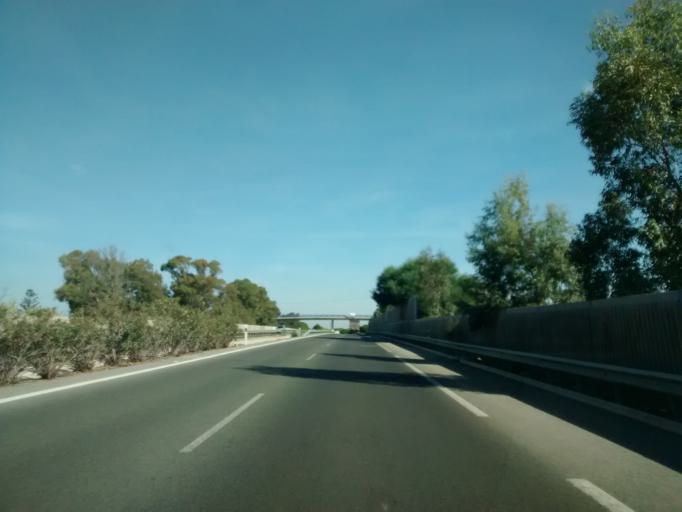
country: ES
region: Andalusia
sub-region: Provincia de Cadiz
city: Chiclana de la Frontera
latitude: 36.3773
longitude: -6.1140
